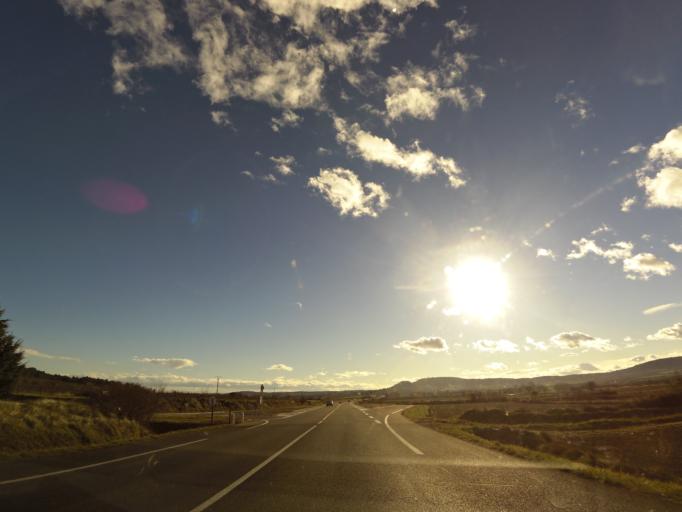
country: FR
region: Languedoc-Roussillon
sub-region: Departement du Gard
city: Nages-et-Solorgues
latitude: 43.8024
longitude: 4.2172
